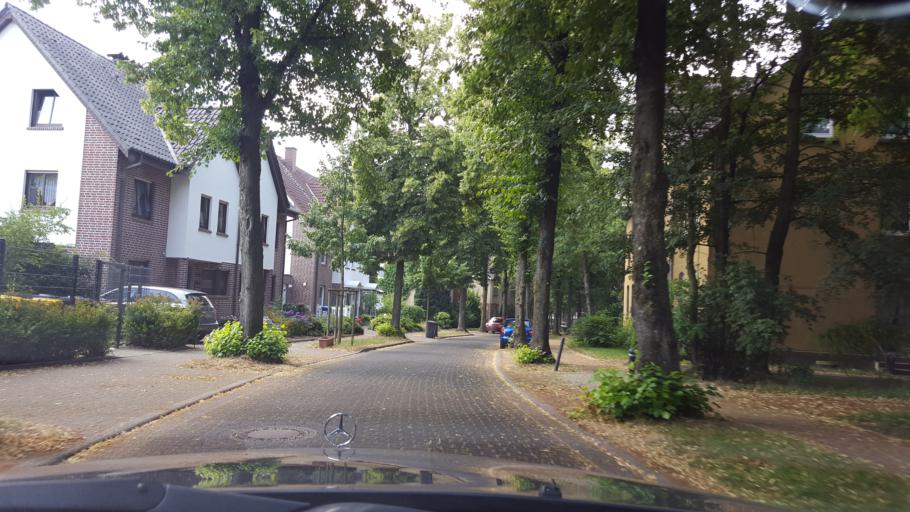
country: DE
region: North Rhine-Westphalia
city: Marl
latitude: 51.6668
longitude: 7.1316
